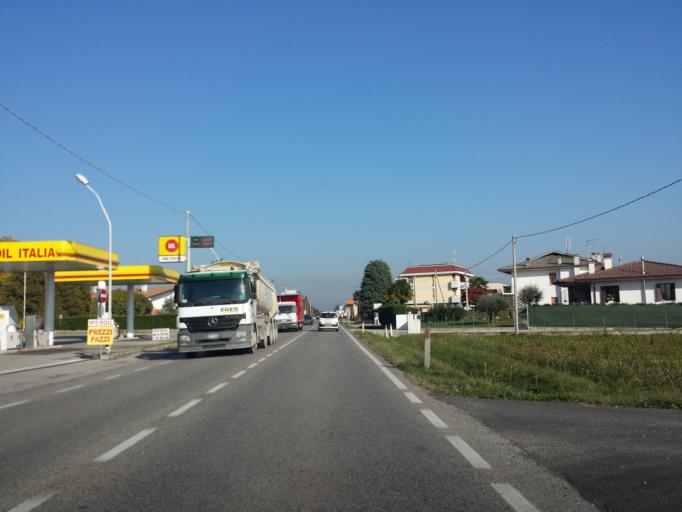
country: IT
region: Veneto
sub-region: Provincia di Treviso
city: Caselle
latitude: 45.7460
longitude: 11.9746
